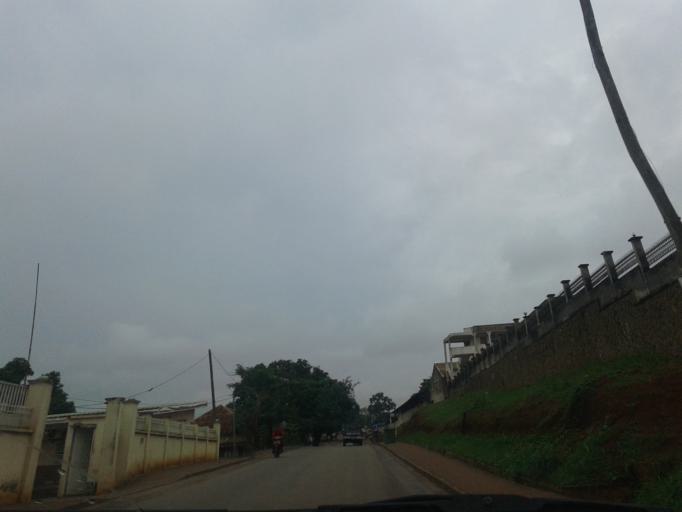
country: CM
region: Centre
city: Yaounde
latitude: 3.8785
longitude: 11.5146
